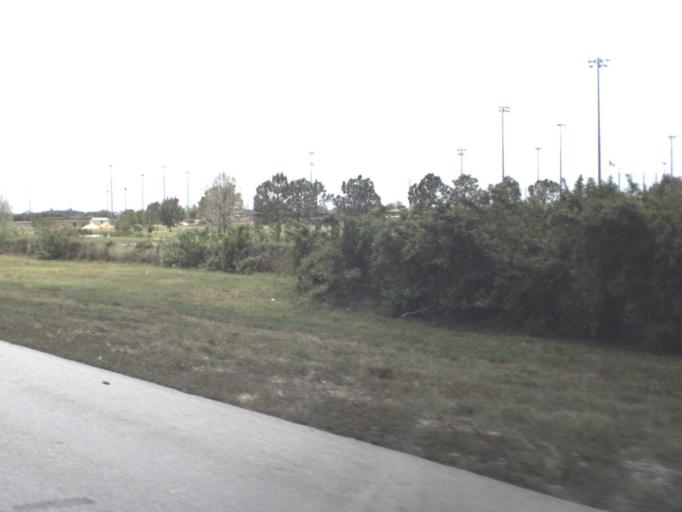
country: US
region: Florida
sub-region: Brevard County
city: Rockledge
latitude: 28.2570
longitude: -80.7264
